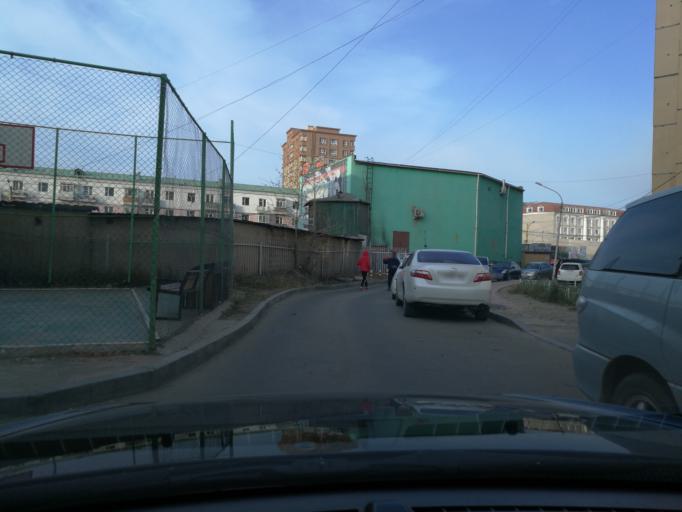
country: MN
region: Ulaanbaatar
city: Ulaanbaatar
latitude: 47.9288
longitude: 106.9221
